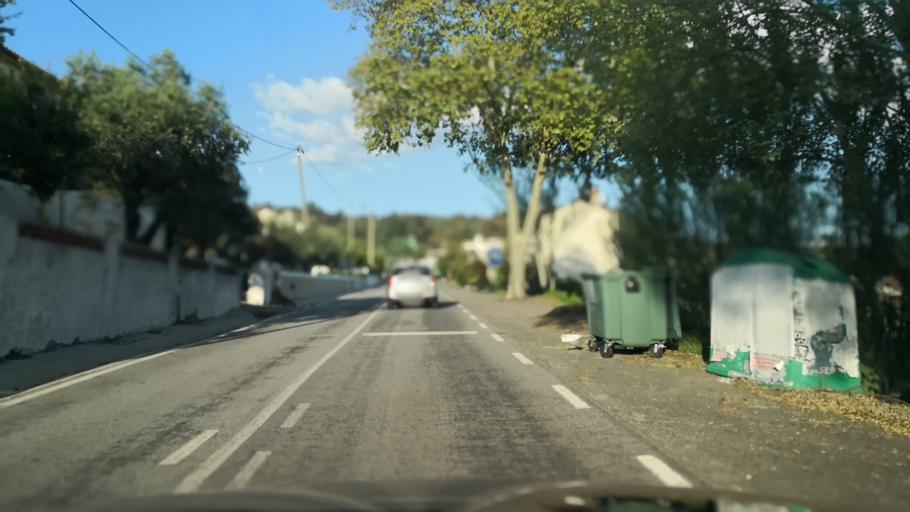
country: PT
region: Portalegre
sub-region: Portalegre
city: Portalegre
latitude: 39.3283
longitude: -7.4313
